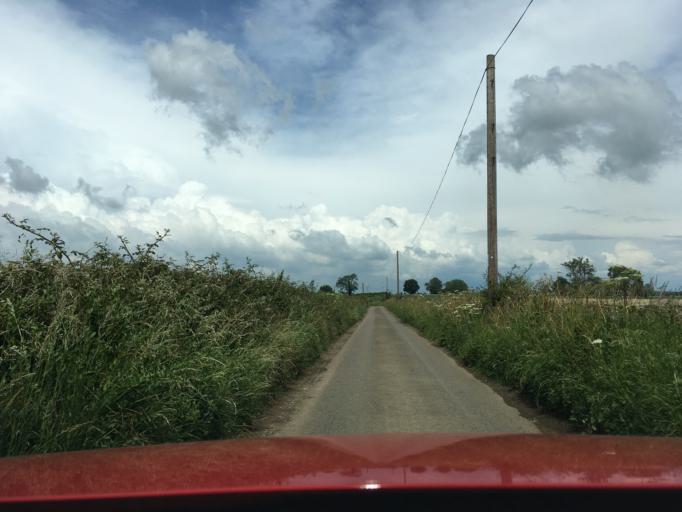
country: GB
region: England
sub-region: Gloucestershire
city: Tetbury
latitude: 51.6667
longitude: -2.1707
